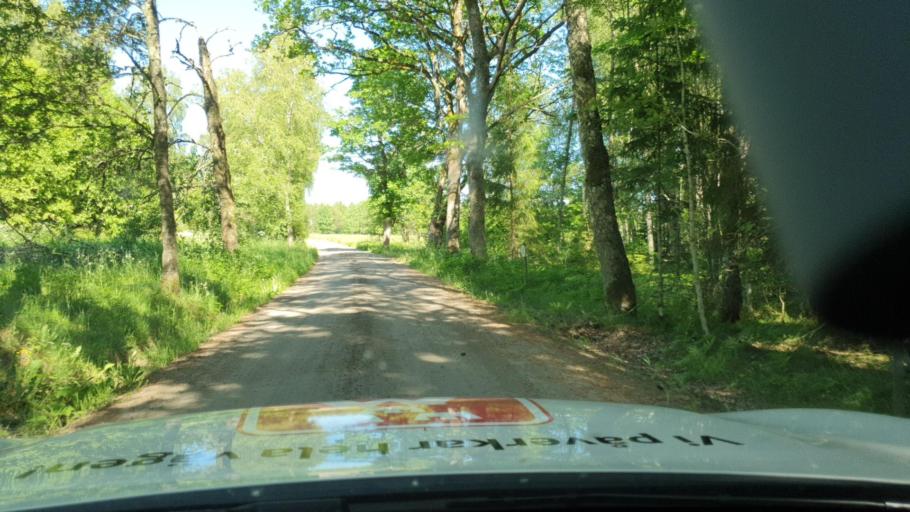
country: SE
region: Vaestra Goetaland
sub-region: Skovde Kommun
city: Skultorp
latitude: 58.3187
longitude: 13.8726
